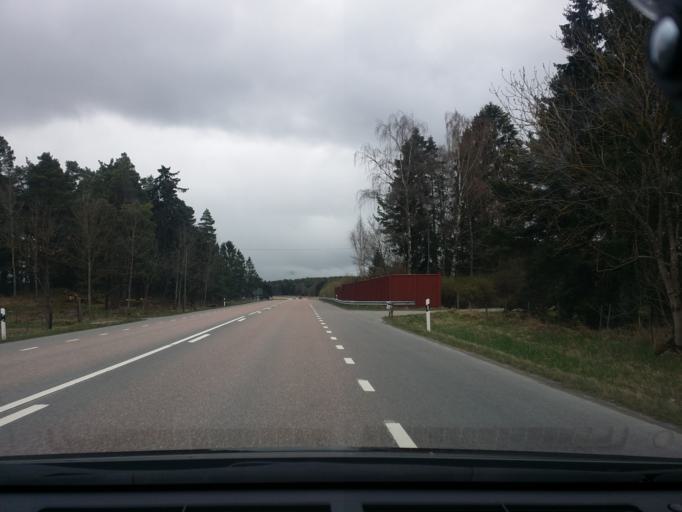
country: SE
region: Uppsala
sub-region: Enkopings Kommun
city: Irsta
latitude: 59.7311
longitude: 16.9578
